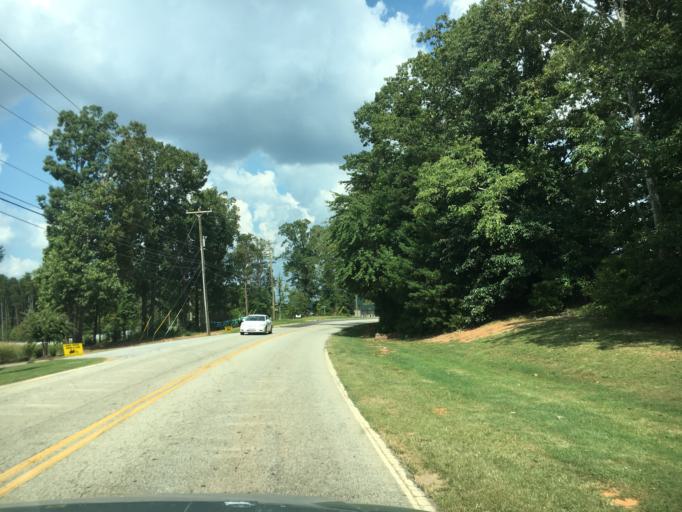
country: US
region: South Carolina
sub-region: Greenville County
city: Mauldin
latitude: 34.8330
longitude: -82.2917
